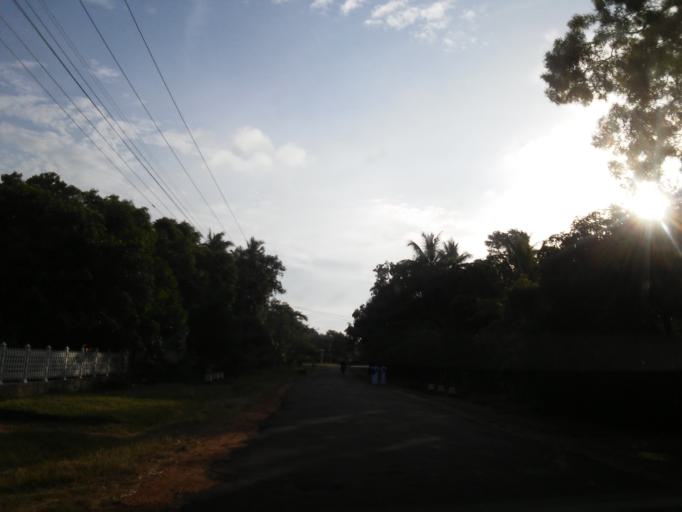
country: LK
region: Central
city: Sigiriya
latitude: 8.1455
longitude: 80.6431
